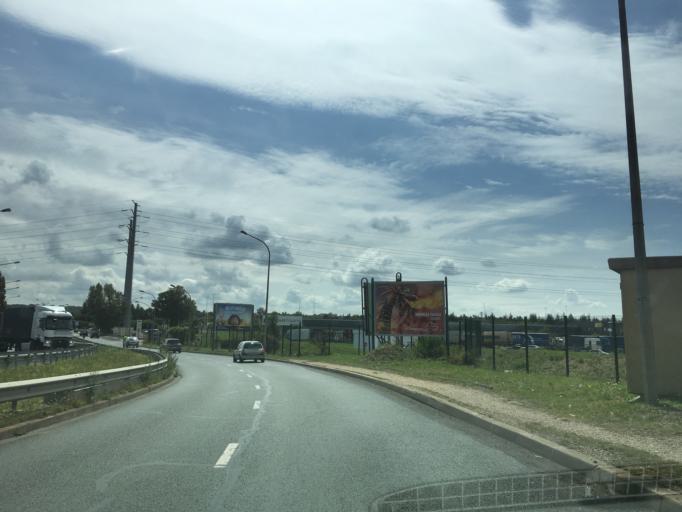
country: FR
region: Ile-de-France
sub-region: Departement du Val-de-Marne
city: Bonneuil-sur-Marne
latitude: 48.7613
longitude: 2.4789
